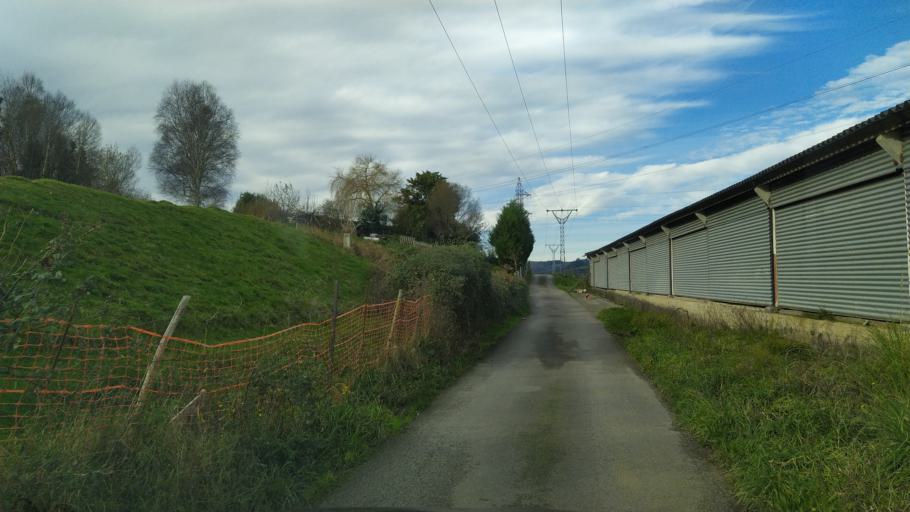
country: ES
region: Cantabria
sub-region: Provincia de Cantabria
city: Reocin
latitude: 43.3541
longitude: -4.0845
